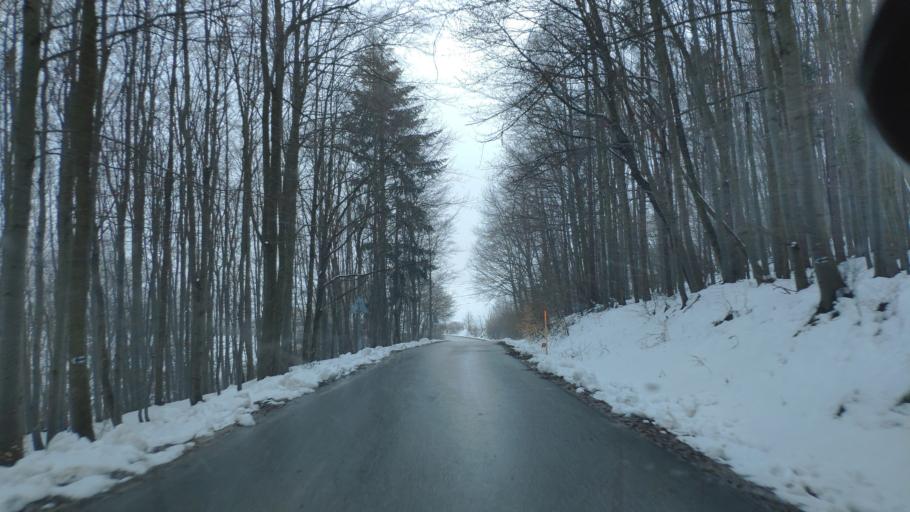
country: SK
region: Nitriansky
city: Stara Tura
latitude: 48.8383
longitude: 17.7060
